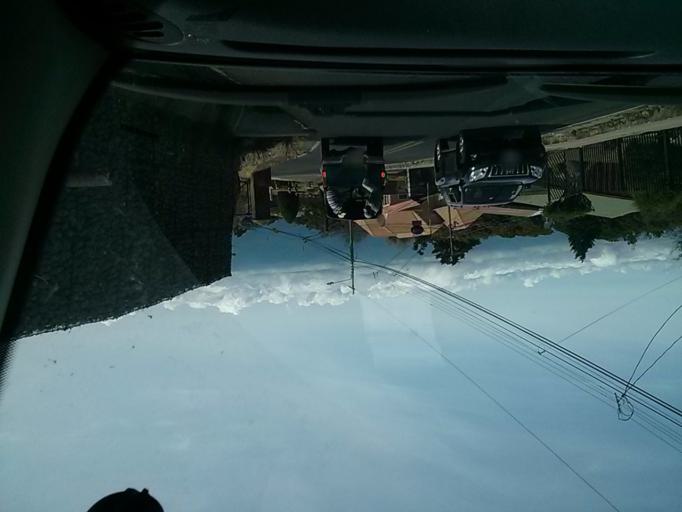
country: CR
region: Cartago
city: Cot
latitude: 9.9204
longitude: -83.8792
